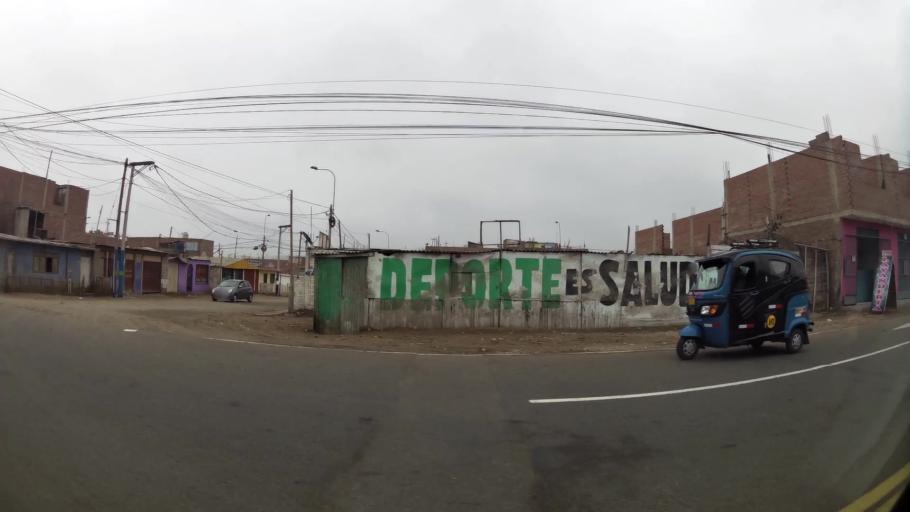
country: PE
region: Lima
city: Ventanilla
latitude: -11.8814
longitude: -77.1286
